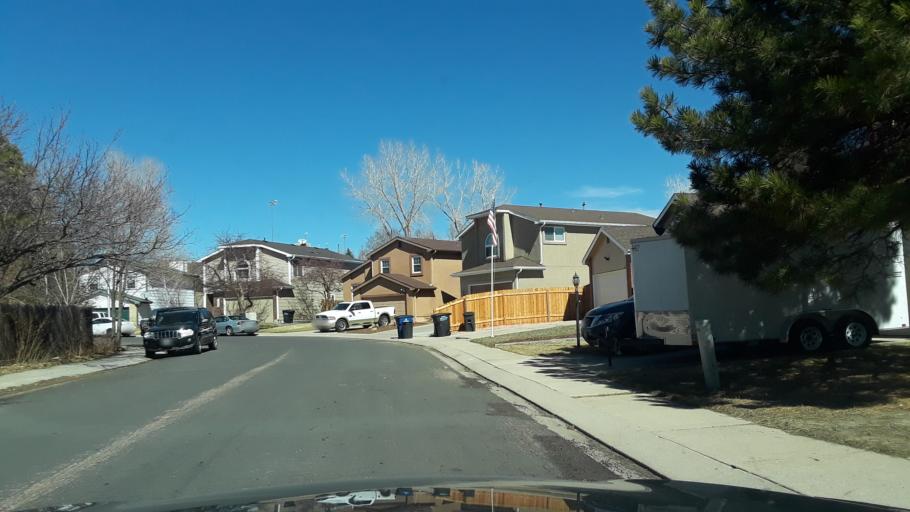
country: US
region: Colorado
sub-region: El Paso County
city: Colorado Springs
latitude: 38.8791
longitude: -104.7969
